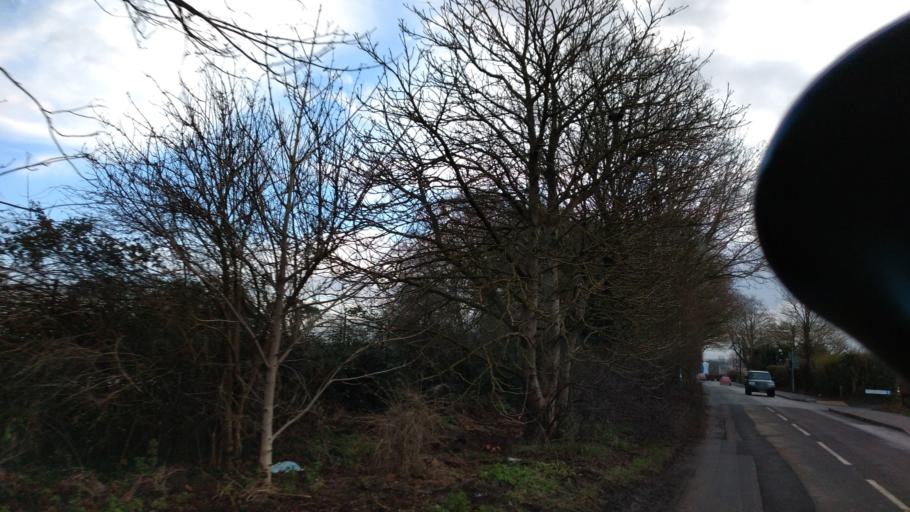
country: GB
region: England
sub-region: Borough of Swindon
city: Highworth
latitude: 51.6257
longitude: -1.7096
